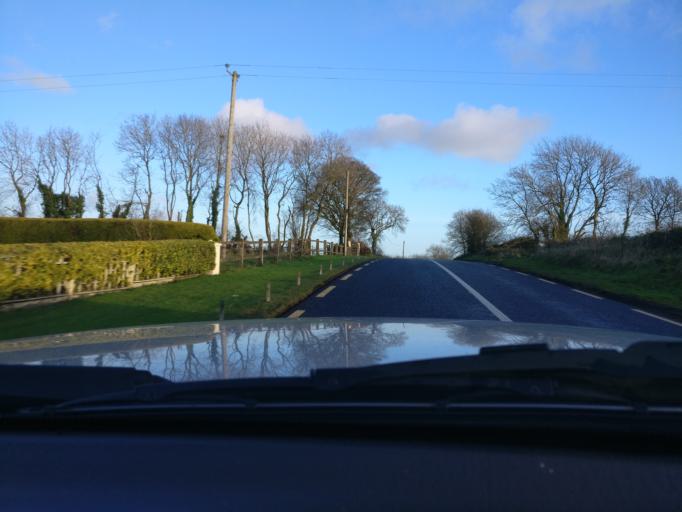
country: IE
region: Leinster
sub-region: An Mhi
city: Navan
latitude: 53.7963
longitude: -6.7009
